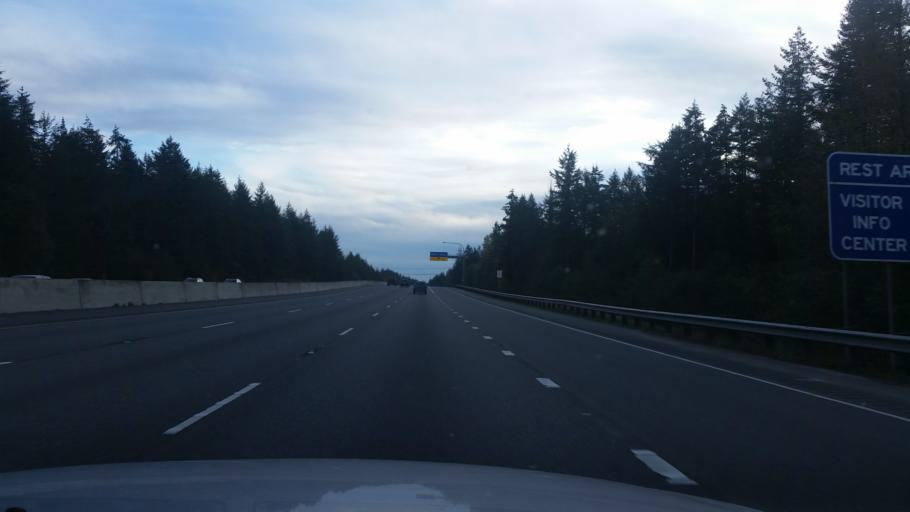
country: US
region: Washington
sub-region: Thurston County
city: Grand Mound
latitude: 46.8764
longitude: -122.9675
